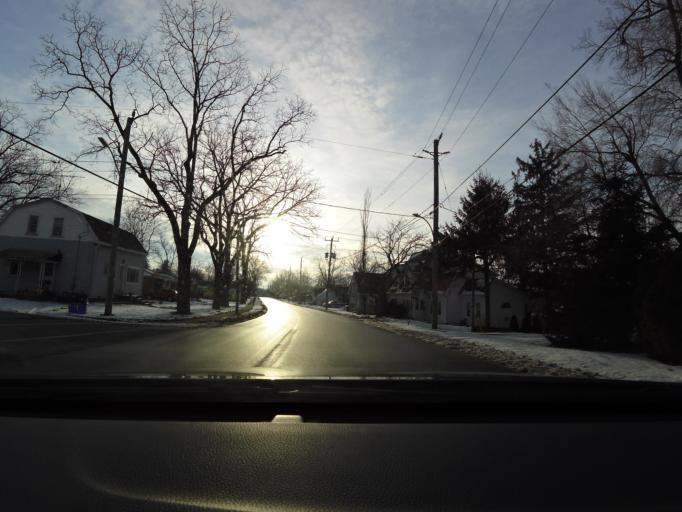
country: CA
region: Ontario
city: Ancaster
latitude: 43.0680
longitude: -79.9389
